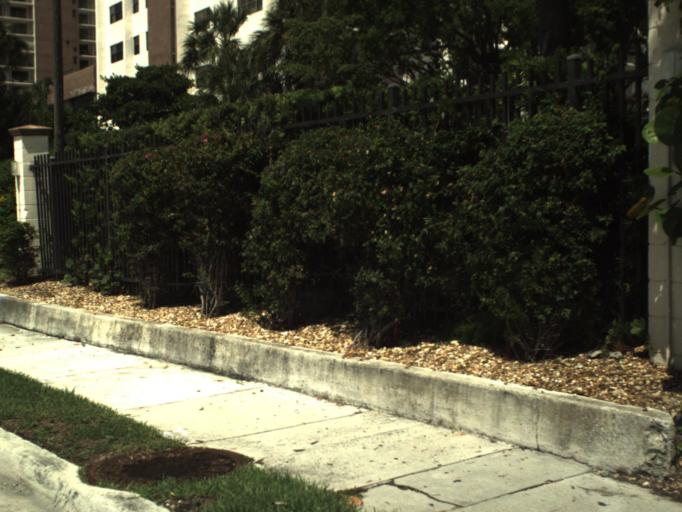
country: US
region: Florida
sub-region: Broward County
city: Hollywood
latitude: 26.0047
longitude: -80.1181
